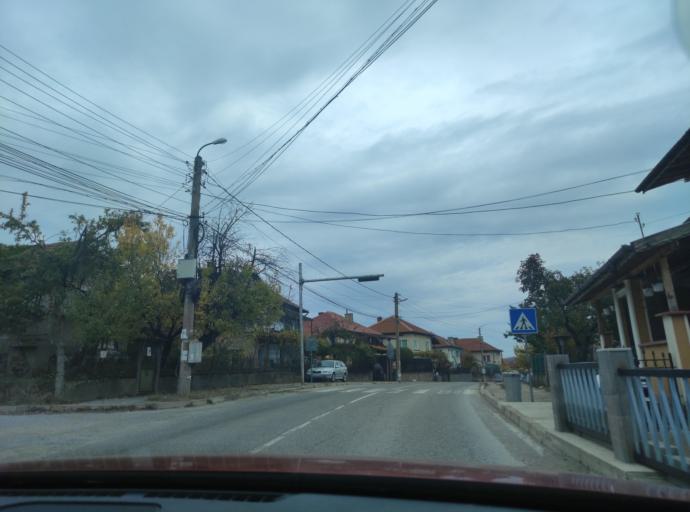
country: BG
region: Montana
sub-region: Obshtina Berkovitsa
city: Berkovitsa
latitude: 43.2049
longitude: 23.1603
